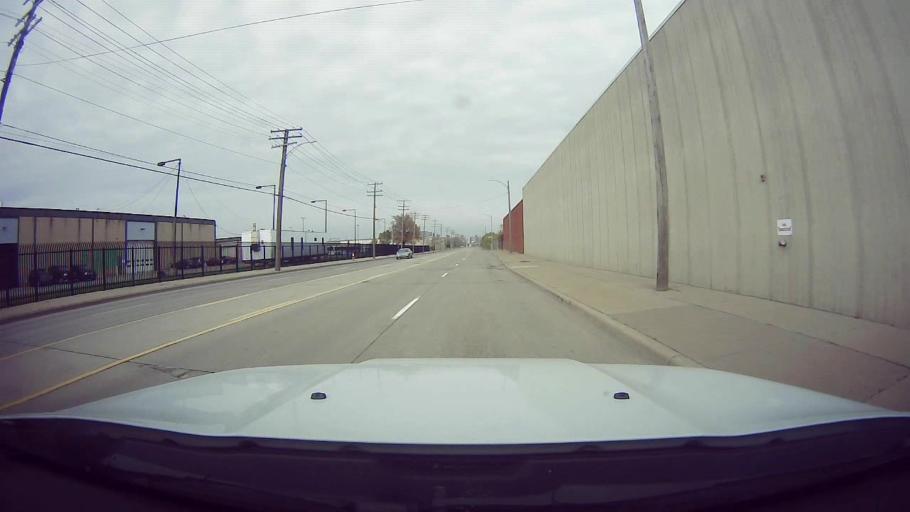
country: US
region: Michigan
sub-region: Wayne County
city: Hamtramck
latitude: 42.3631
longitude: -83.0515
